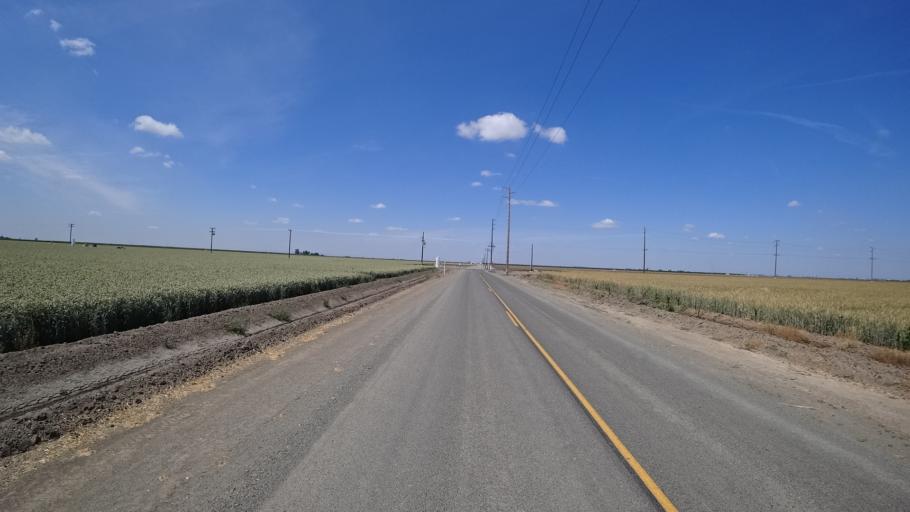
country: US
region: California
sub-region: Tulare County
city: Goshen
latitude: 36.2833
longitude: -119.4910
